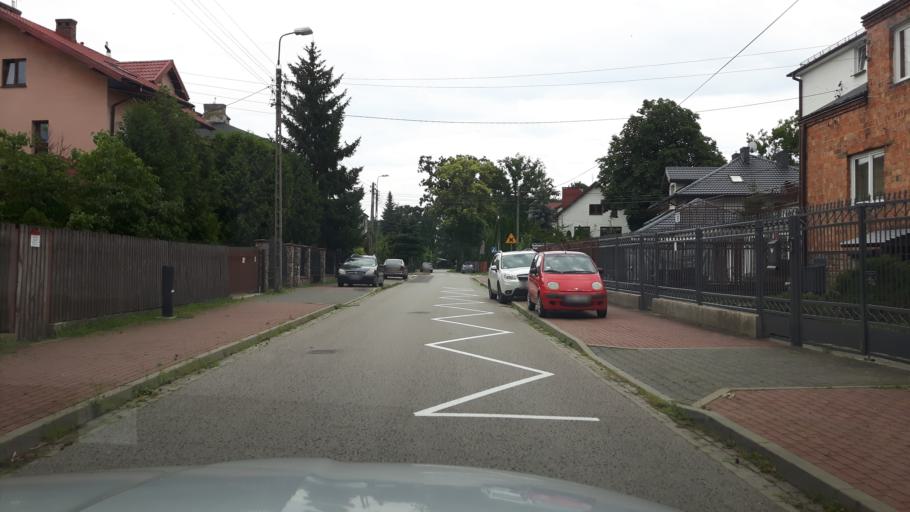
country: PL
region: Masovian Voivodeship
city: Zielonka
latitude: 52.3083
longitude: 21.1601
